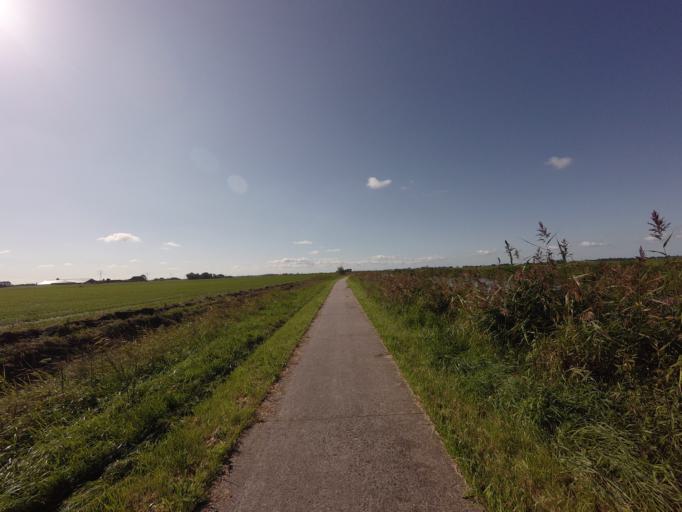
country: NL
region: Friesland
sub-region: Gemeente Boarnsterhim
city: Reduzum
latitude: 53.1399
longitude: 5.7625
